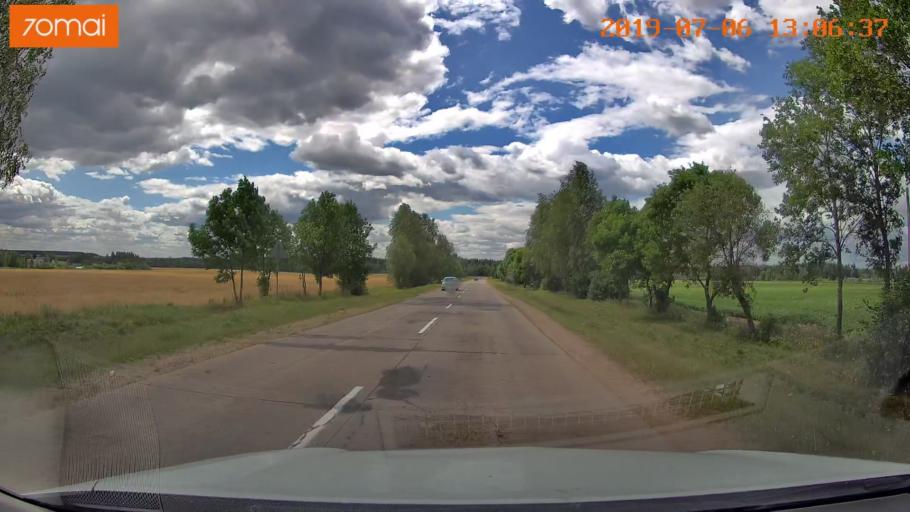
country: BY
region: Minsk
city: Dzyarzhynsk
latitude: 53.6796
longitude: 27.0508
